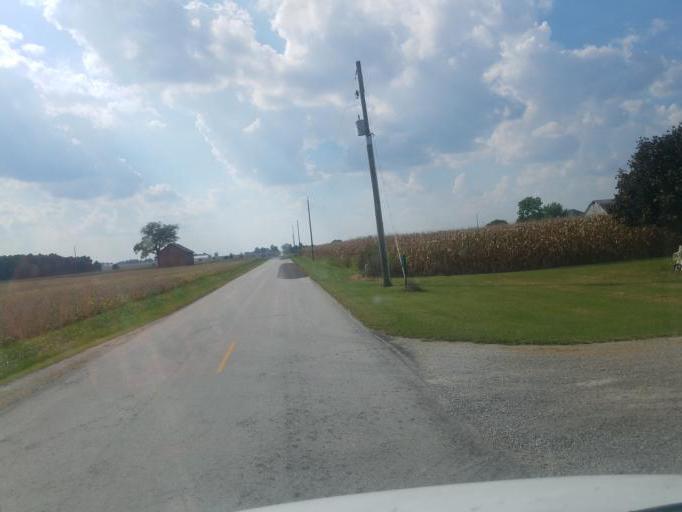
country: US
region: Ohio
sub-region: Hardin County
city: Kenton
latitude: 40.7463
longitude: -83.6291
